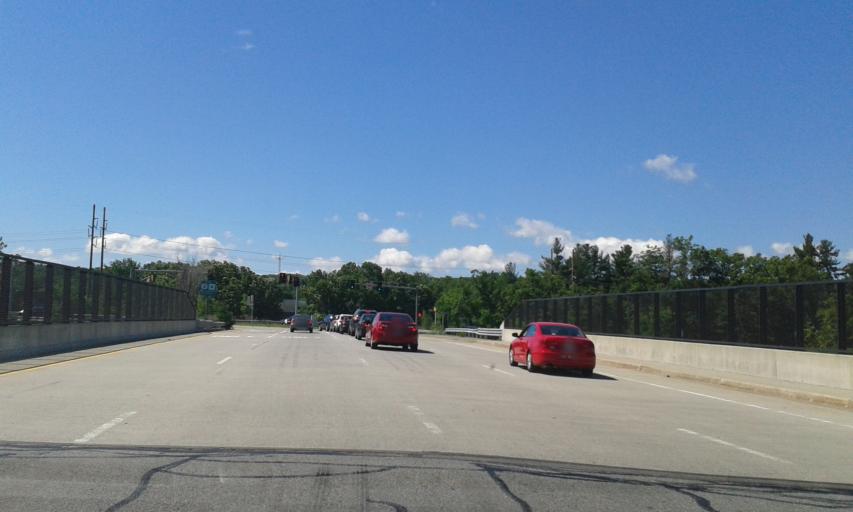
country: US
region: Massachusetts
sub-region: Middlesex County
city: Chelmsford
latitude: 42.6229
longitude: -71.3671
